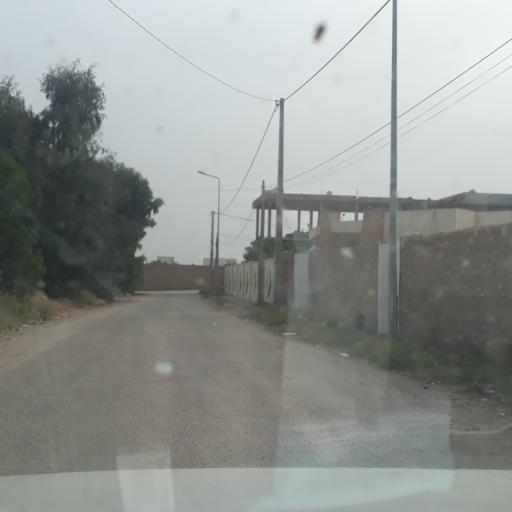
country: TN
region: Safaqis
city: Al Qarmadah
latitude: 34.8214
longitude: 10.7756
